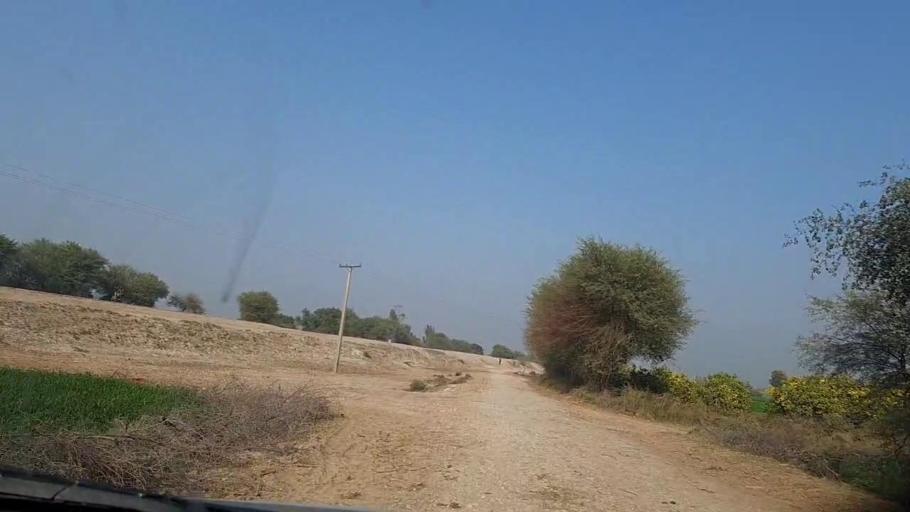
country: PK
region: Sindh
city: Moro
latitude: 26.8034
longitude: 67.9482
